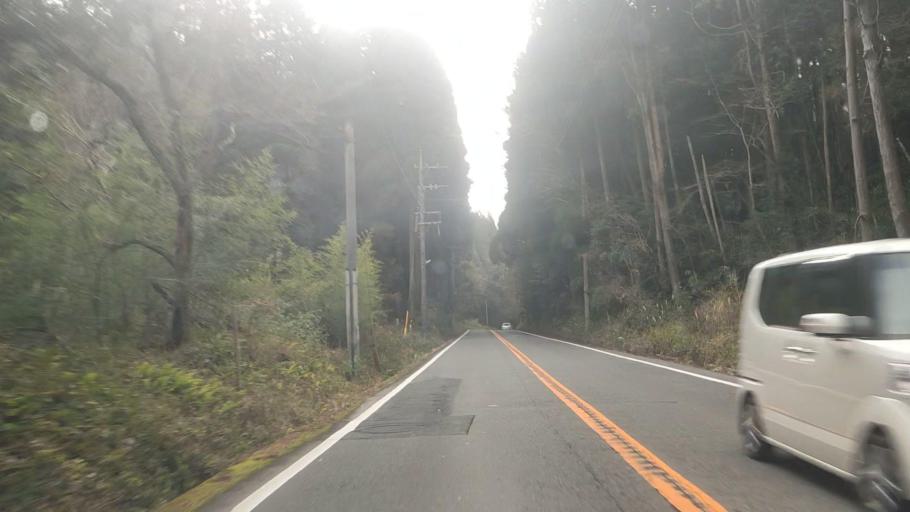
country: JP
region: Kagoshima
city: Kajiki
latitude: 31.8744
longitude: 130.6872
